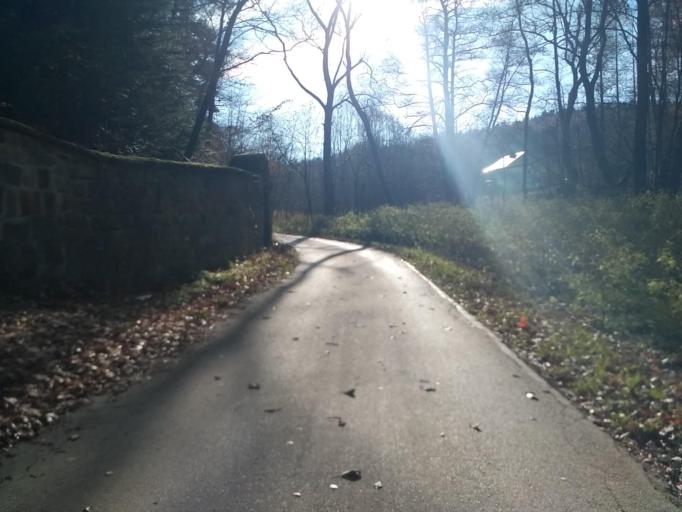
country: PL
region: Subcarpathian Voivodeship
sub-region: Powiat brzozowski
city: Turze Pole
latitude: 49.6852
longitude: 21.9972
